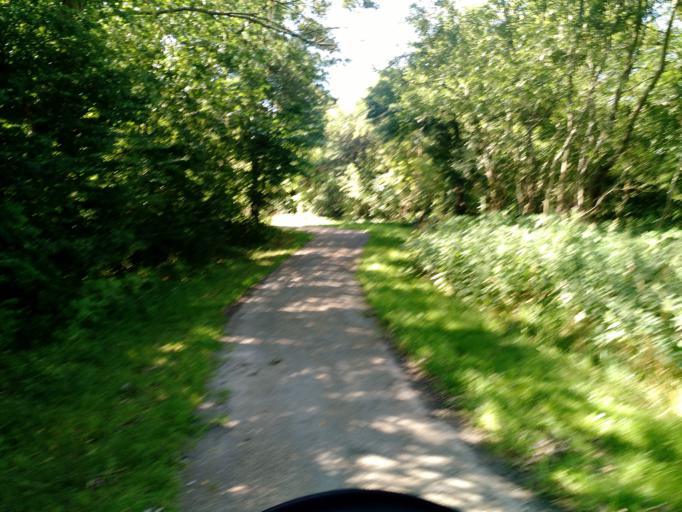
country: DK
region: Capital Region
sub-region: Herlev Kommune
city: Herlev
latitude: 55.7514
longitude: 12.4250
